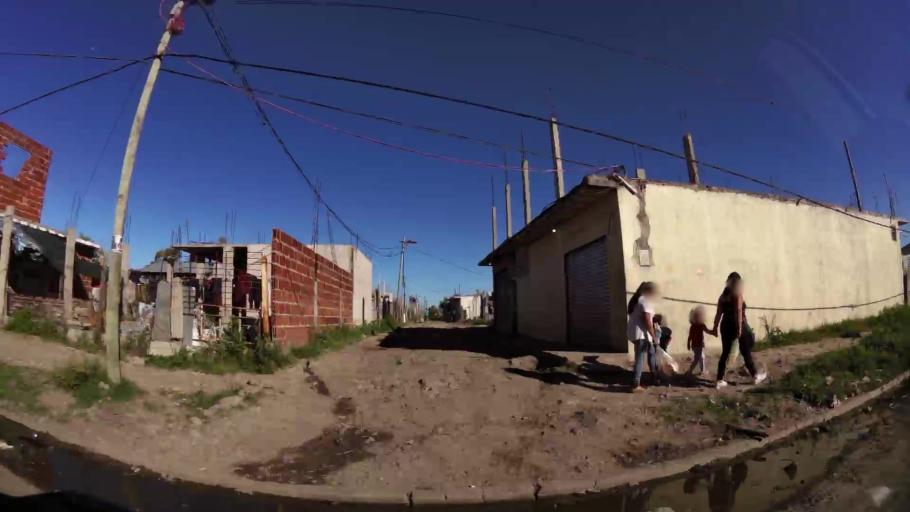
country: AR
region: Buenos Aires
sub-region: Partido de Quilmes
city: Quilmes
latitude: -34.7492
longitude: -58.3140
